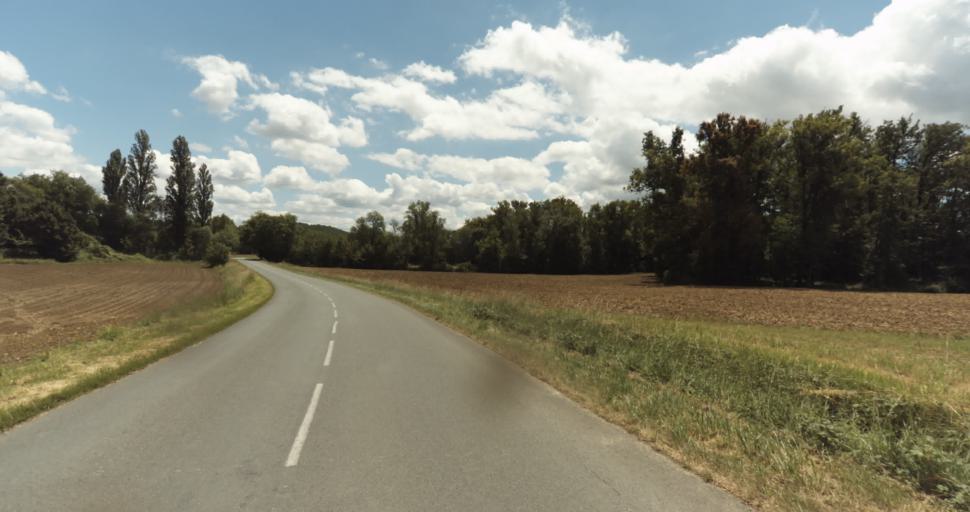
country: FR
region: Aquitaine
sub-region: Departement du Lot-et-Garonne
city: Villereal
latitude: 44.6806
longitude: 0.7611
